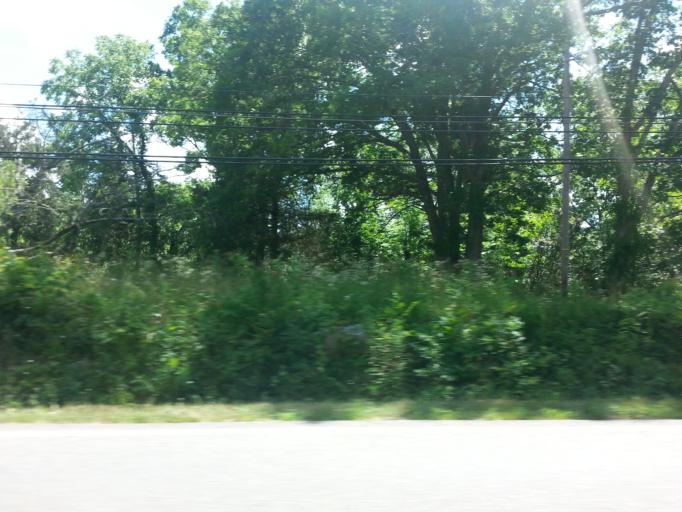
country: US
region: Virginia
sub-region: Lee County
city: Pennington Gap
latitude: 36.7203
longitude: -82.9828
